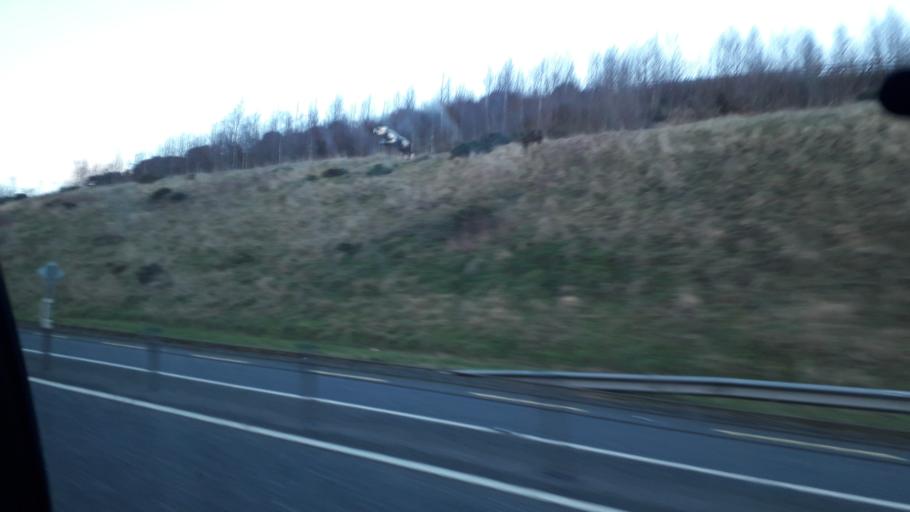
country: IE
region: Ulster
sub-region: County Monaghan
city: Castleblayney
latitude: 54.1297
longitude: -6.7711
